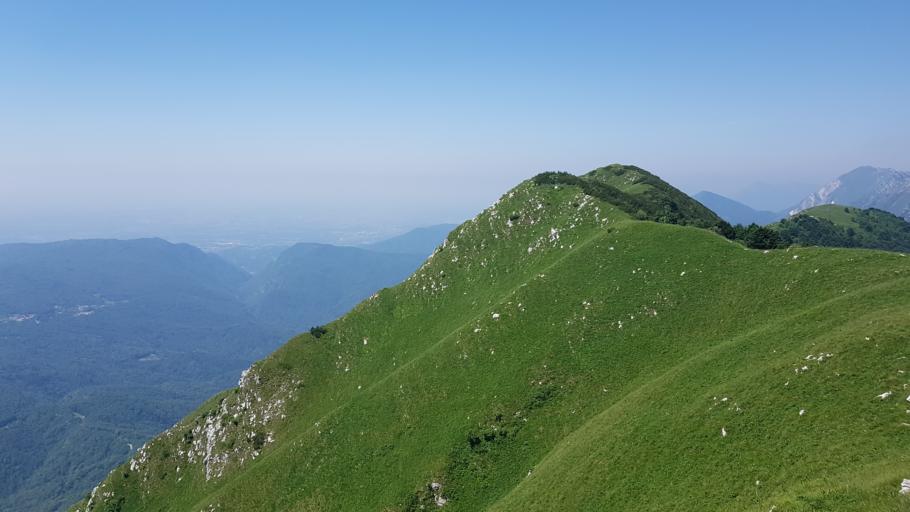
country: IT
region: Friuli Venezia Giulia
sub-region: Provincia di Udine
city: Lusevera
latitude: 46.2908
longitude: 13.3118
